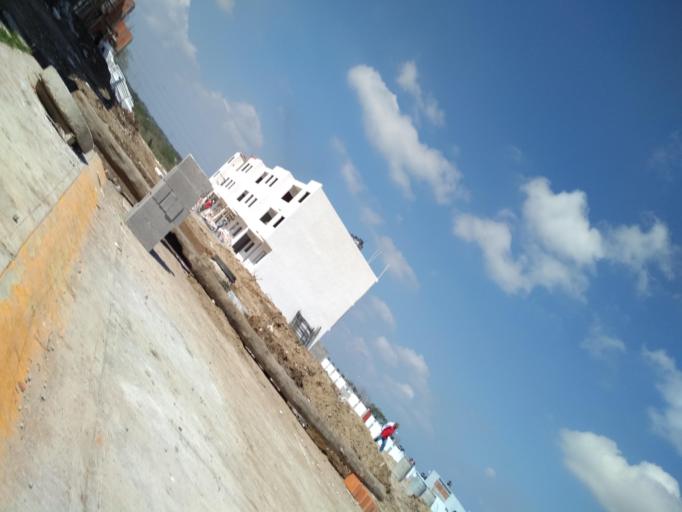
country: MX
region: Veracruz
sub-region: Veracruz
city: Las Amapolas
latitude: 19.1374
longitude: -96.2219
